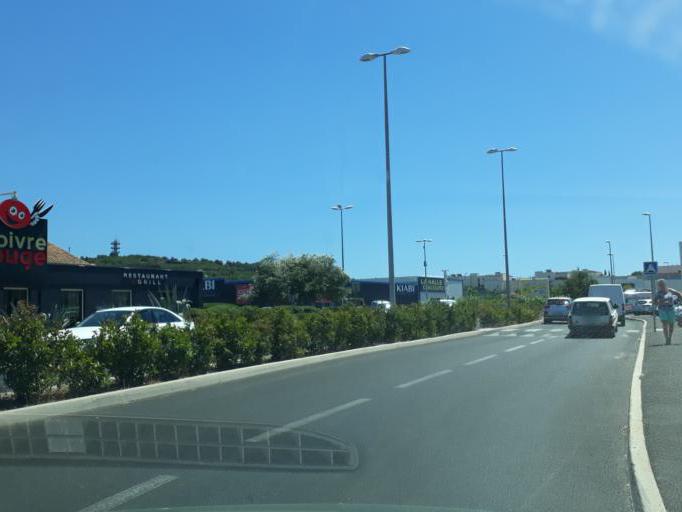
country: FR
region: Languedoc-Roussillon
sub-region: Departement de l'Herault
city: Agde
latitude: 43.3076
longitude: 3.4919
